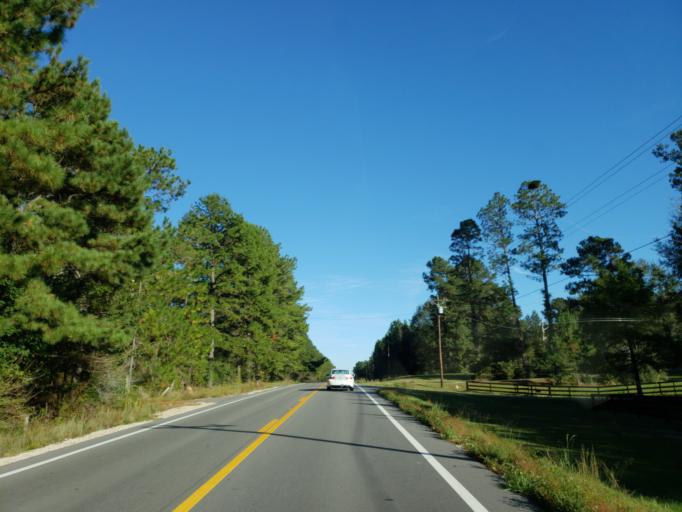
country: US
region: Mississippi
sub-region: Perry County
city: Richton
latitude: 31.3700
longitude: -89.0712
